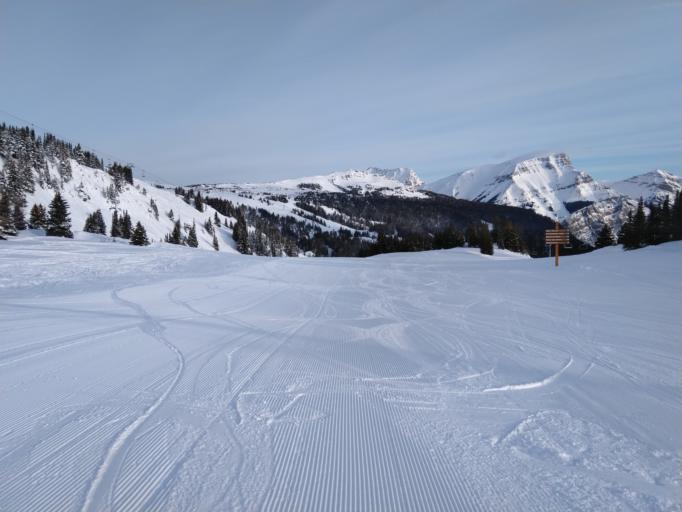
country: CA
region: Alberta
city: Banff
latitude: 51.0716
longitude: -115.7825
